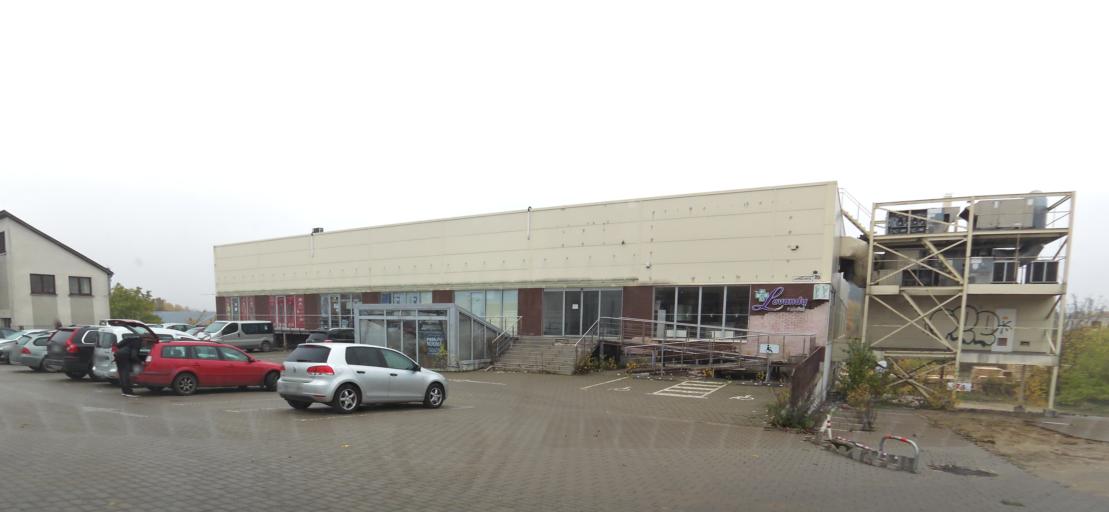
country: LT
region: Vilnius County
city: Rasos
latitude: 54.6606
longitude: 25.3037
